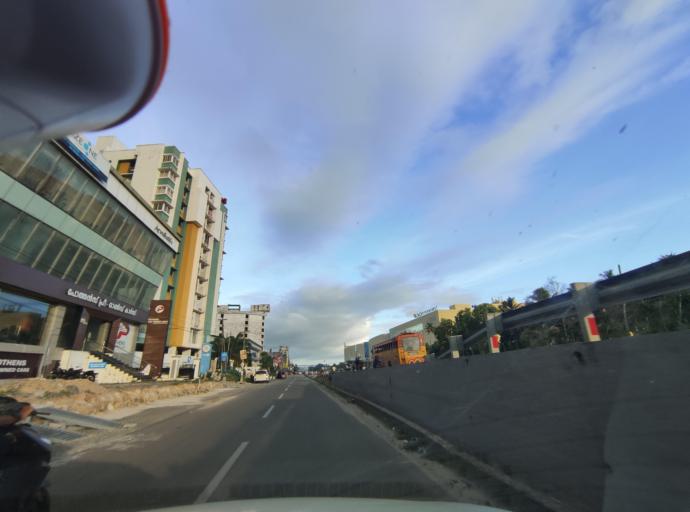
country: IN
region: Kerala
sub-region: Thiruvananthapuram
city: Thiruvananthapuram
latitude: 8.5192
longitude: 76.8957
